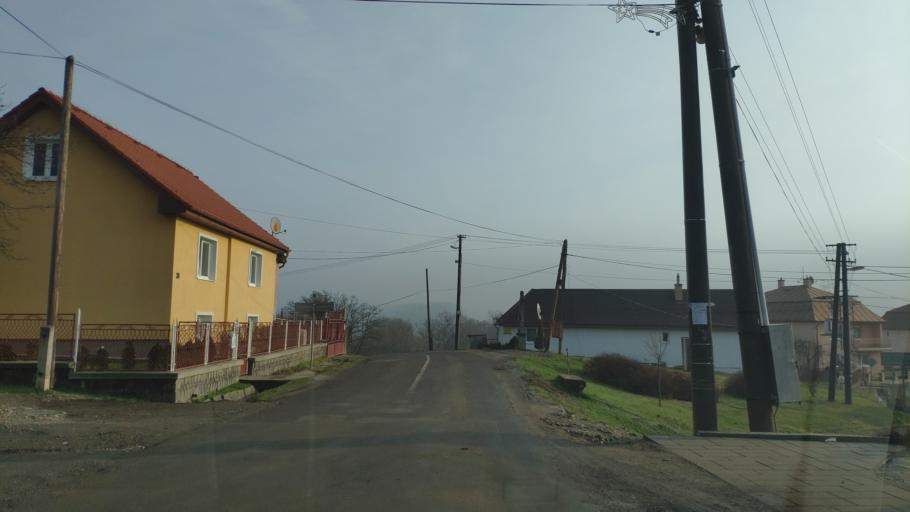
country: SK
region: Kosicky
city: Kosice
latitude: 48.7053
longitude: 21.4115
